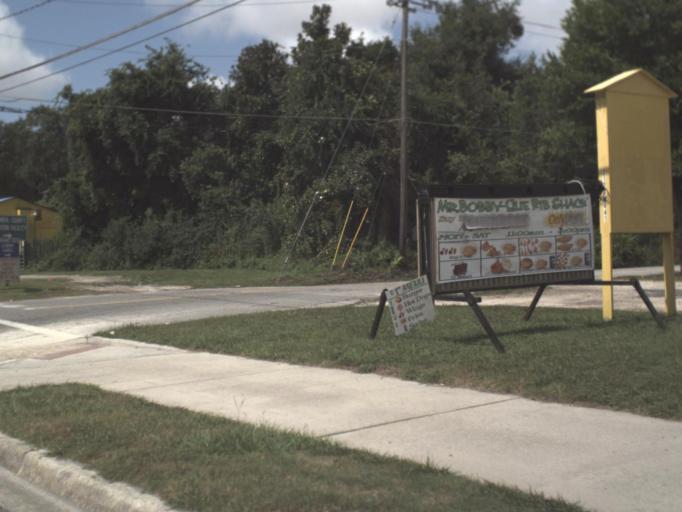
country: US
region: Florida
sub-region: Columbia County
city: Five Points
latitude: 30.2187
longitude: -82.6382
